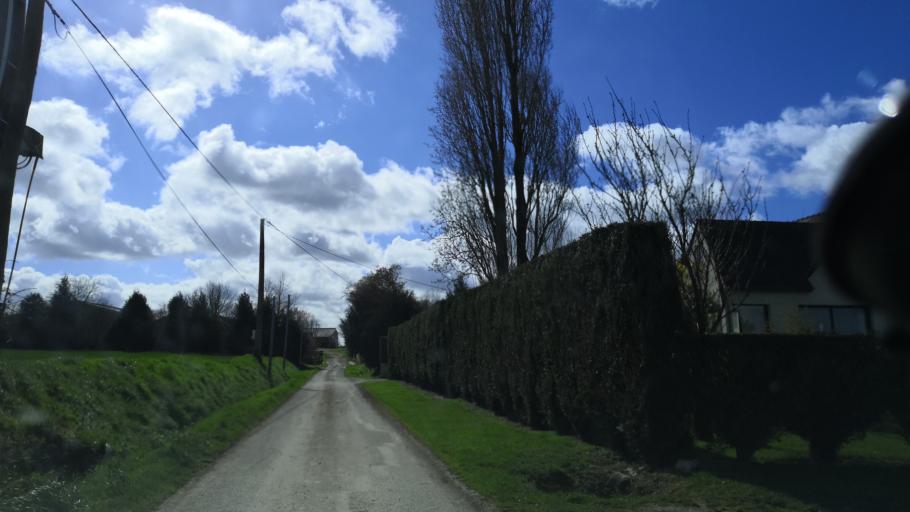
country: FR
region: Brittany
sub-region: Departement d'Ille-et-Vilaine
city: Bedee
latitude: 48.1830
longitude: -1.9750
